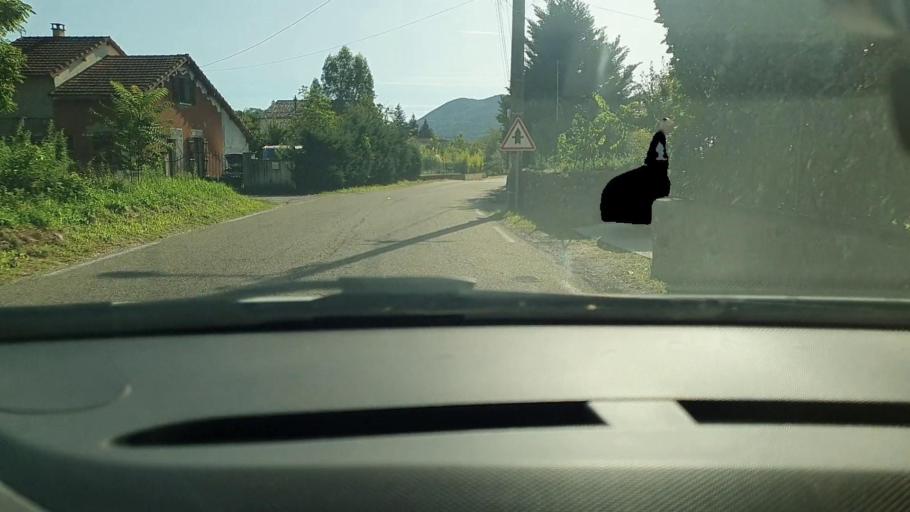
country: FR
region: Languedoc-Roussillon
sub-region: Departement du Gard
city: Saint-Florent-sur-Auzonnet
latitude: 44.2449
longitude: 4.1000
